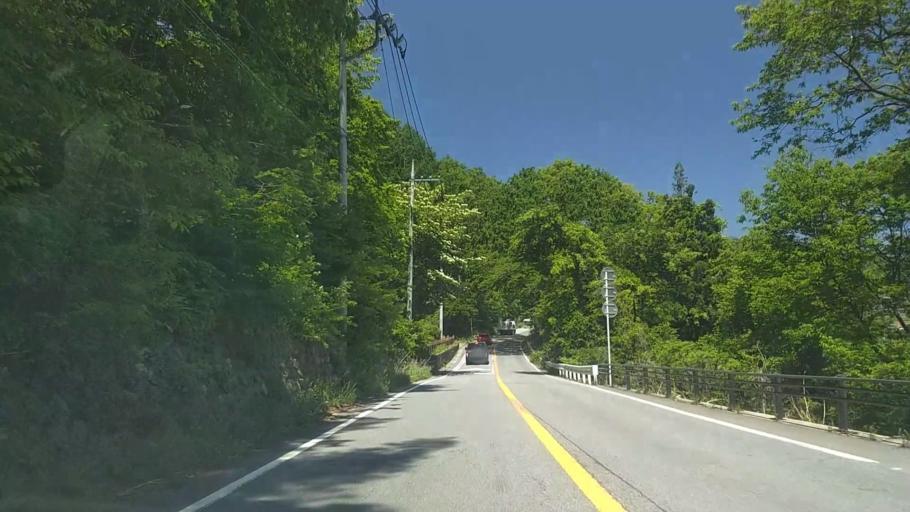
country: JP
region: Yamanashi
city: Nirasaki
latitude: 35.8606
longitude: 138.4294
